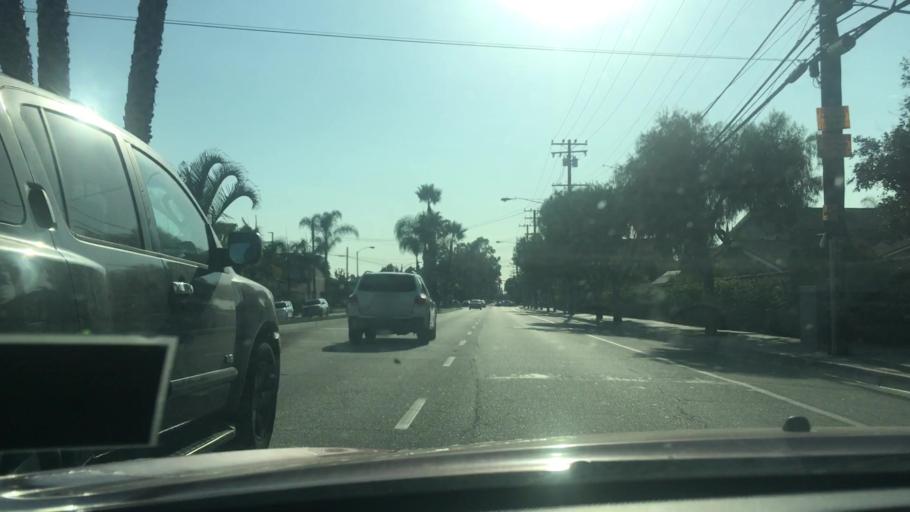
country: US
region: California
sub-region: Los Angeles County
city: Artesia
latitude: 33.8731
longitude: -118.0887
